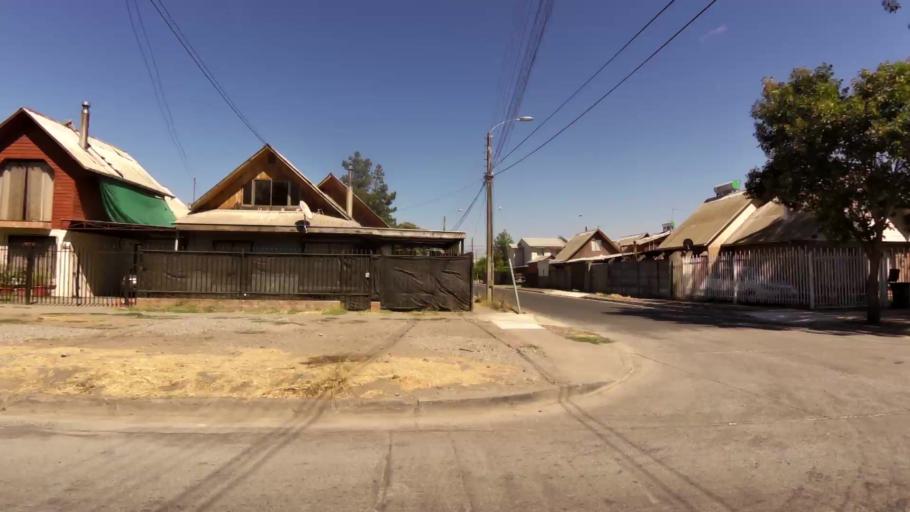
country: CL
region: Maule
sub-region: Provincia de Curico
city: Curico
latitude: -34.9739
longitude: -71.2526
